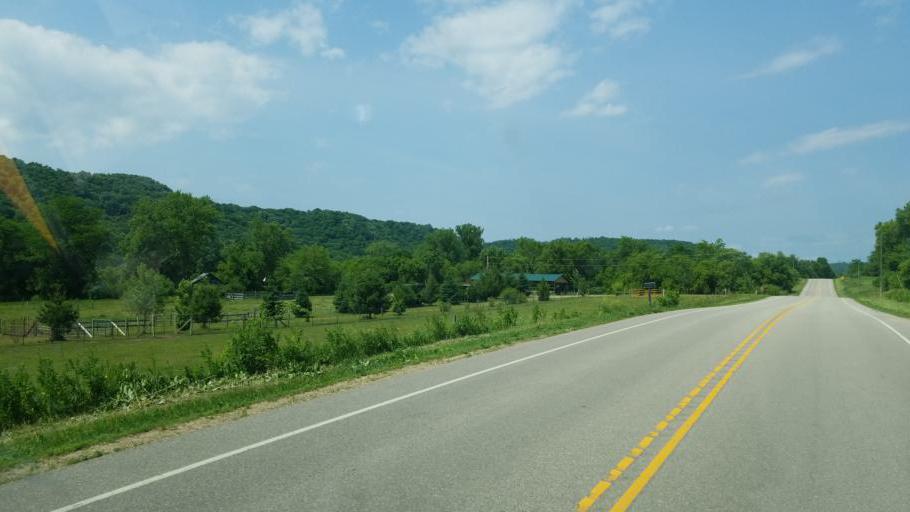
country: US
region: Wisconsin
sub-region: Vernon County
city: Viroqua
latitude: 43.4803
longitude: -90.6916
